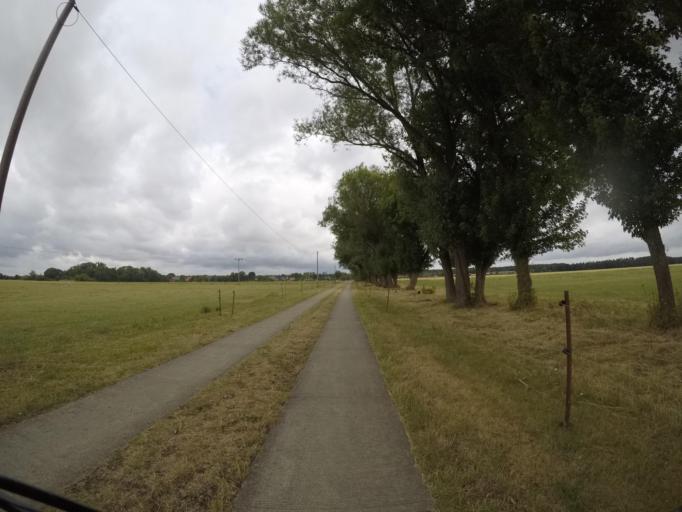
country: DE
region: Lower Saxony
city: Hitzacker
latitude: 53.1761
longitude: 11.1112
